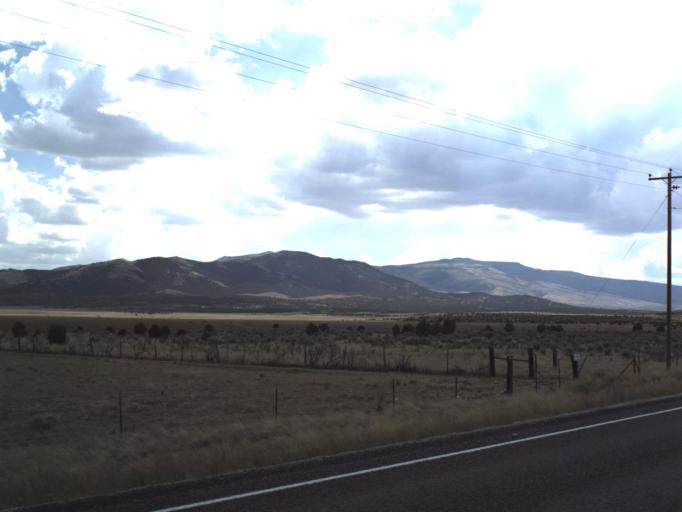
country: US
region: Idaho
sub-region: Minidoka County
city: Rupert
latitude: 41.9709
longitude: -113.1327
